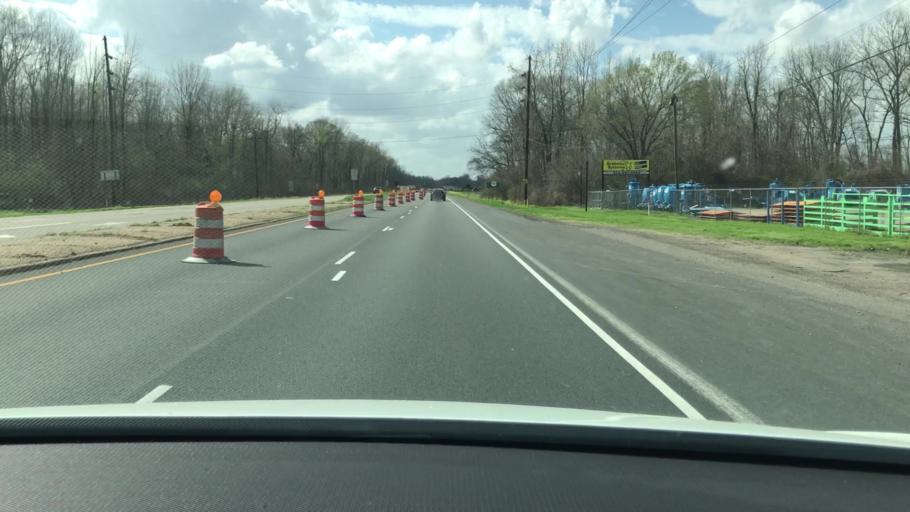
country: US
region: Louisiana
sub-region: Pointe Coupee Parish
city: Livonia
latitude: 30.5572
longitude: -91.6422
